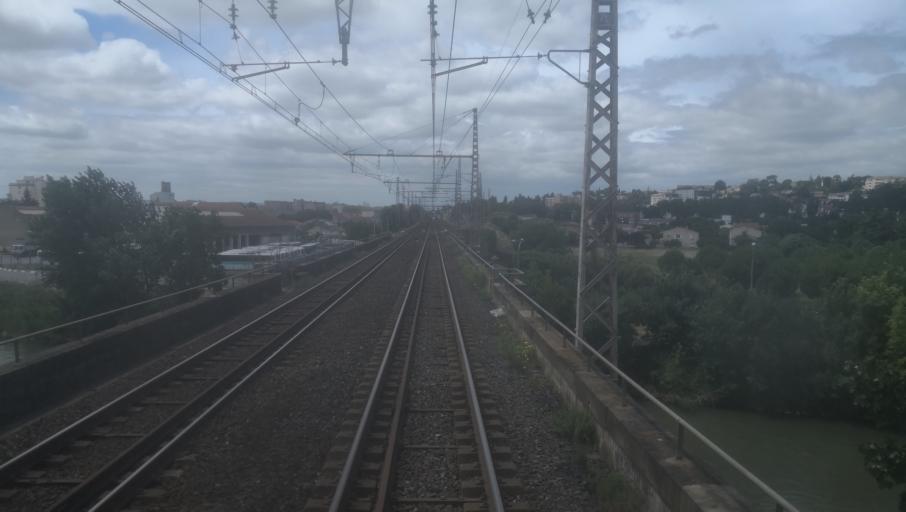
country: FR
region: Languedoc-Roussillon
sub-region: Departement de l'Aude
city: Carcassonne
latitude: 43.2188
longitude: 2.3627
